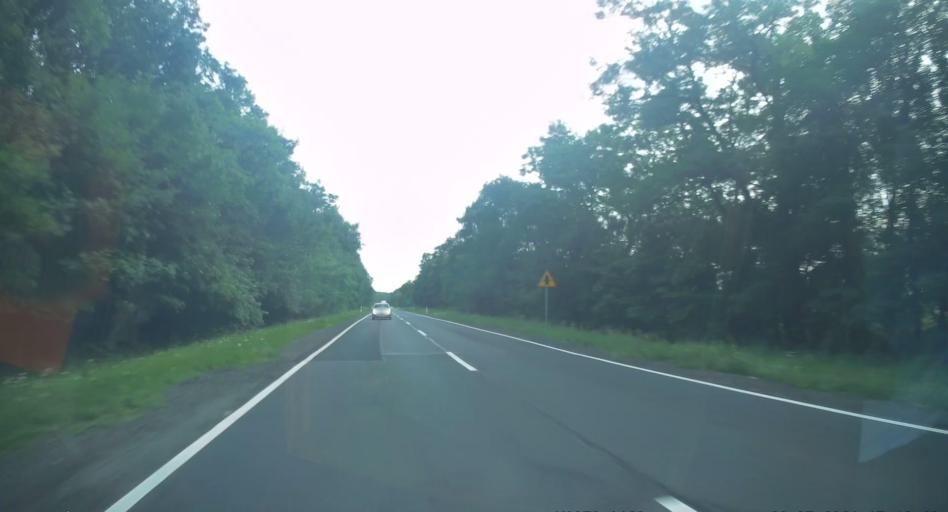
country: PL
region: Lodz Voivodeship
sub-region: Powiat radomszczanski
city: Plawno
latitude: 50.9641
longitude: 19.4056
